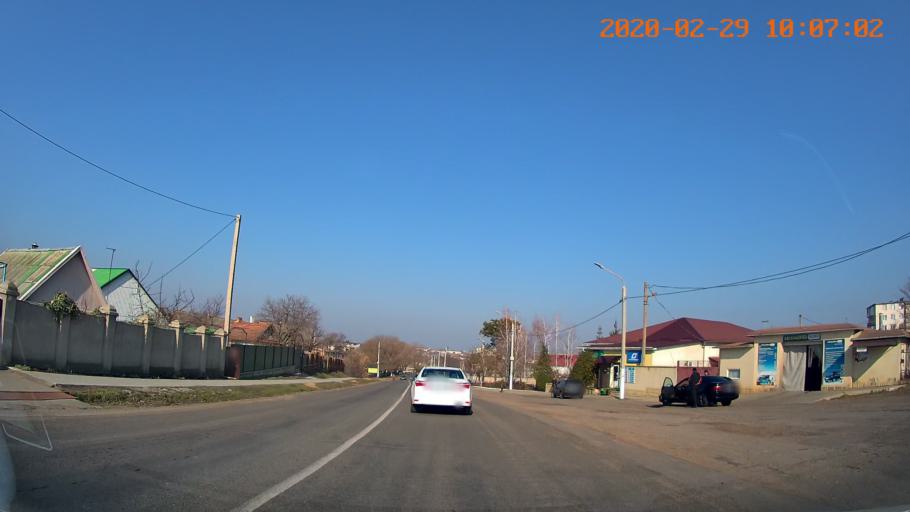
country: MD
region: Telenesti
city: Tiraspolul Nou
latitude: 46.8190
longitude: 29.6677
